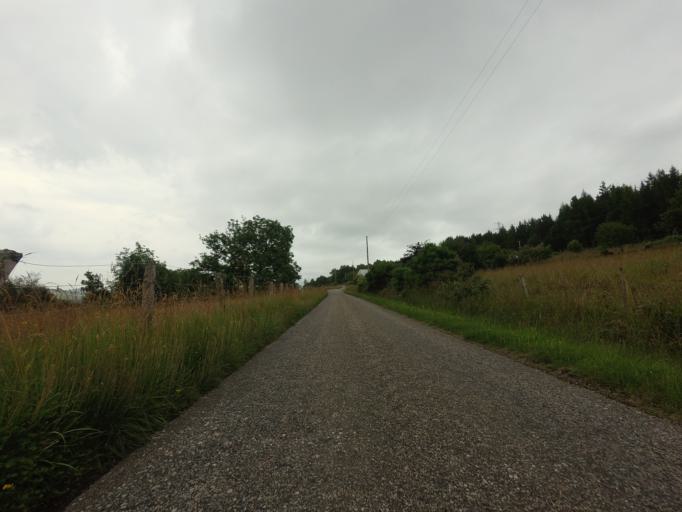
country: GB
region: Scotland
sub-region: Highland
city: Evanton
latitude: 57.9035
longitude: -4.3876
